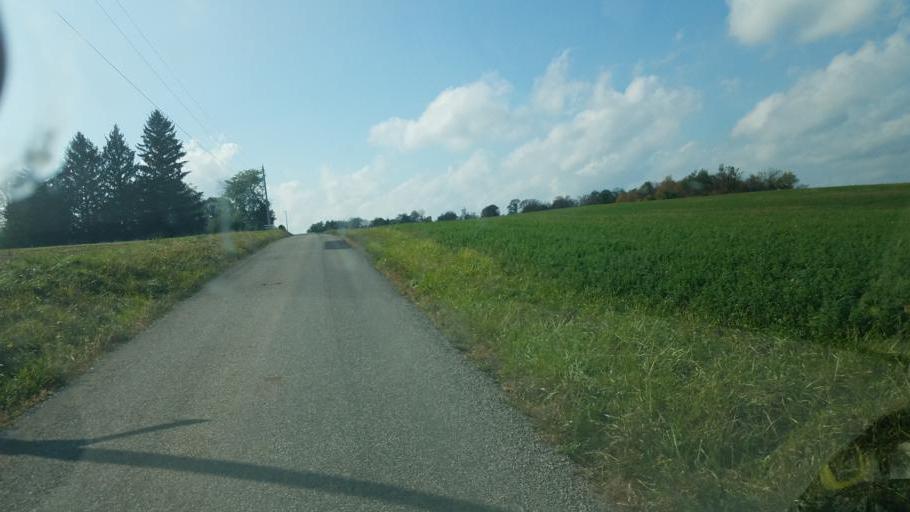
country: US
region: Ohio
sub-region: Holmes County
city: Millersburg
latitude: 40.6307
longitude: -81.8653
